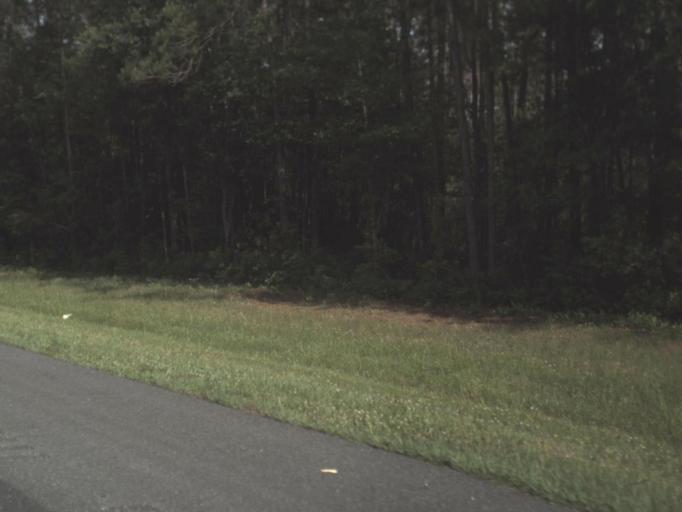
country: US
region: Florida
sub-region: Baker County
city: Macclenny
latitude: 30.2339
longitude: -82.2842
